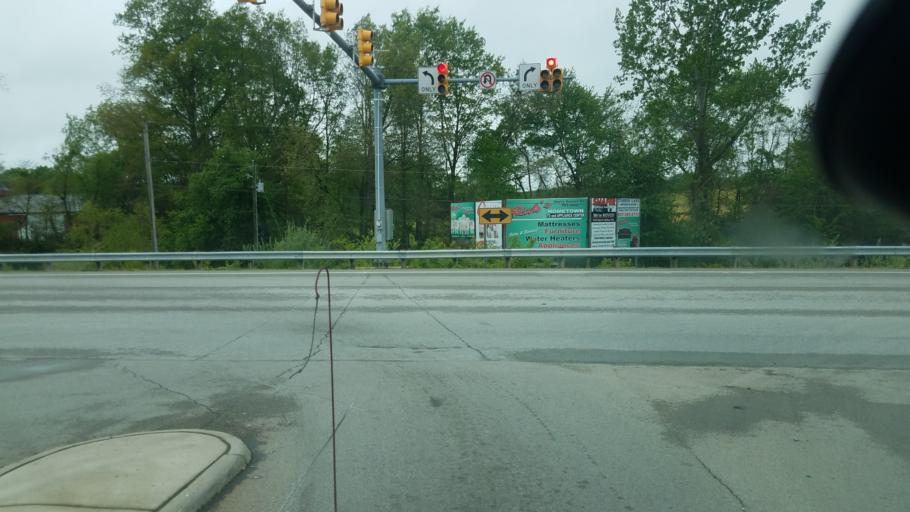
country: US
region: Ohio
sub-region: Highland County
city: Hillsboro
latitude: 39.2248
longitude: -83.6246
